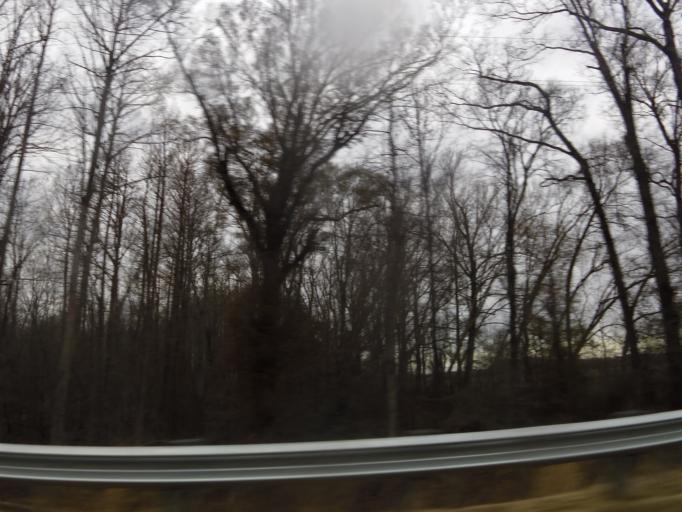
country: US
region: North Carolina
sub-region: Halifax County
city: Scotland Neck
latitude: 36.2343
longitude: -77.3582
